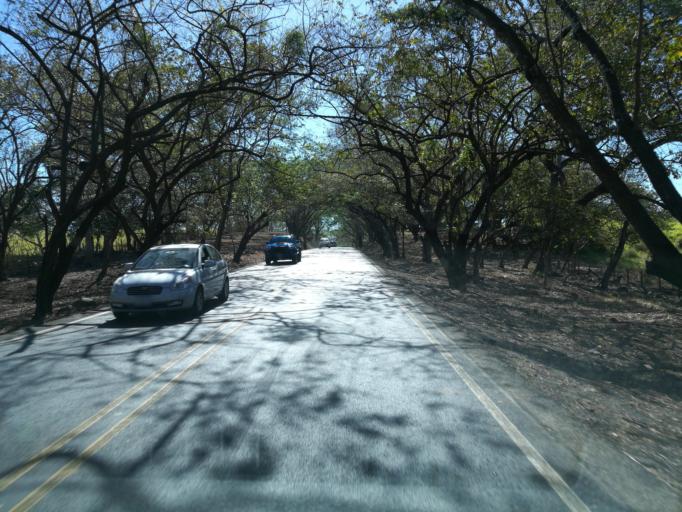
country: CR
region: Puntarenas
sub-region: Canton Central de Puntarenas
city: Puntarenas
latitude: 10.1064
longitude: -84.8809
